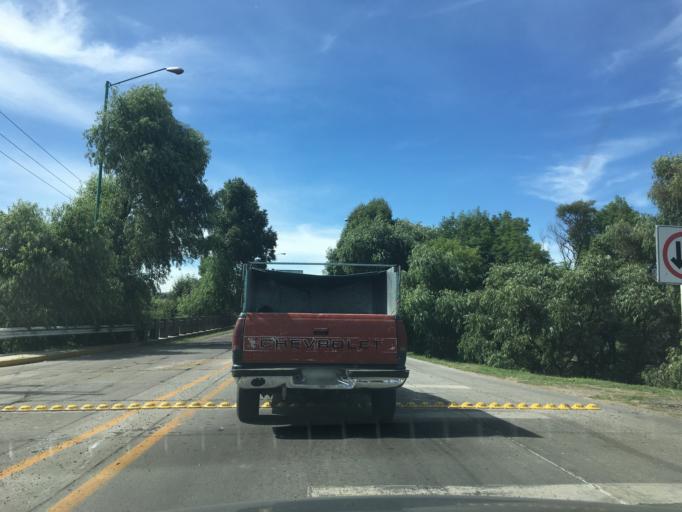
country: MX
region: Guanajuato
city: Coroneo
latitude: 20.1954
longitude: -100.3661
